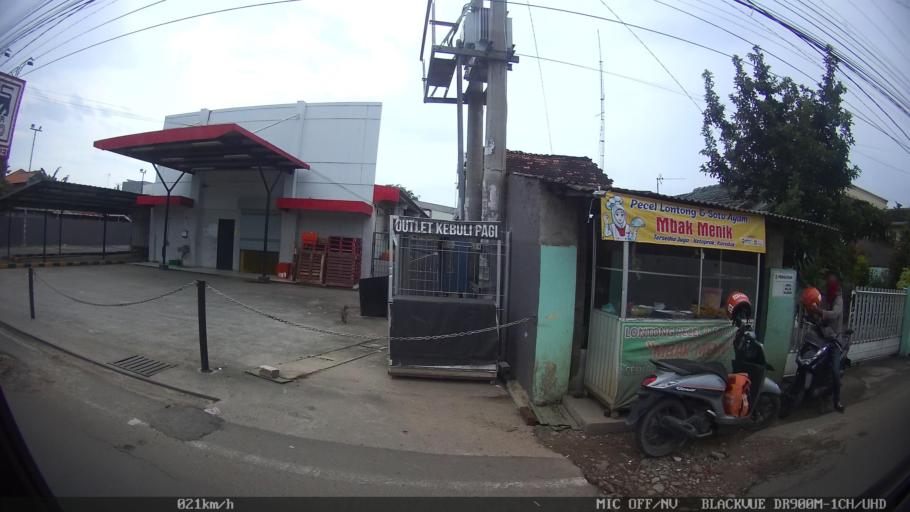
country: ID
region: Lampung
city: Kedaton
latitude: -5.3802
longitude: 105.2527
